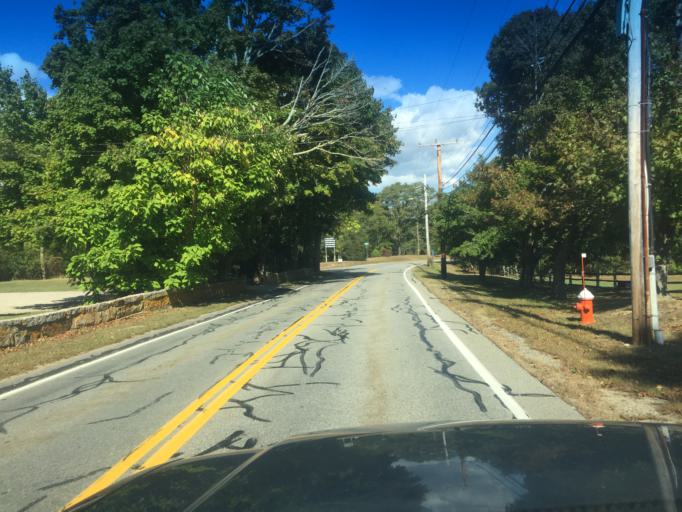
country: US
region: Massachusetts
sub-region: Barnstable County
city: Pocasset
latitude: 41.6737
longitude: -70.6095
